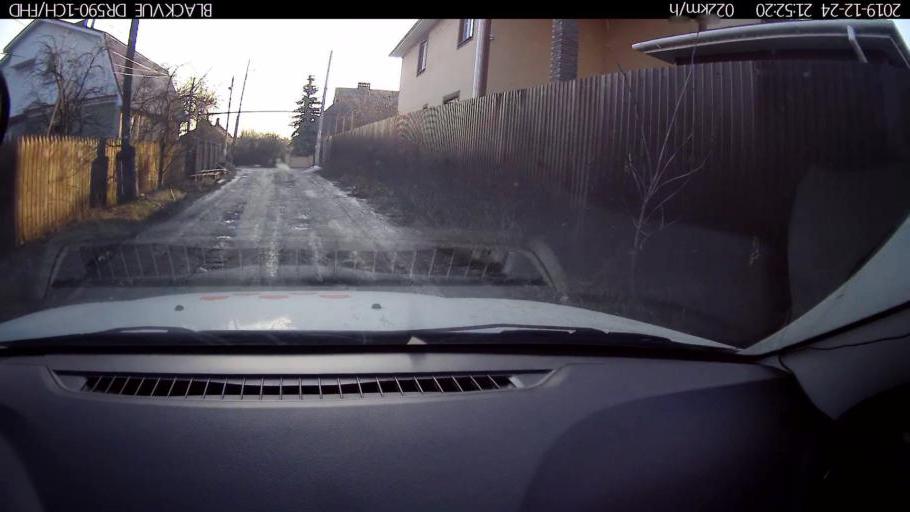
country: RU
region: Nizjnij Novgorod
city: Burevestnik
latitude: 56.2178
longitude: 43.8460
